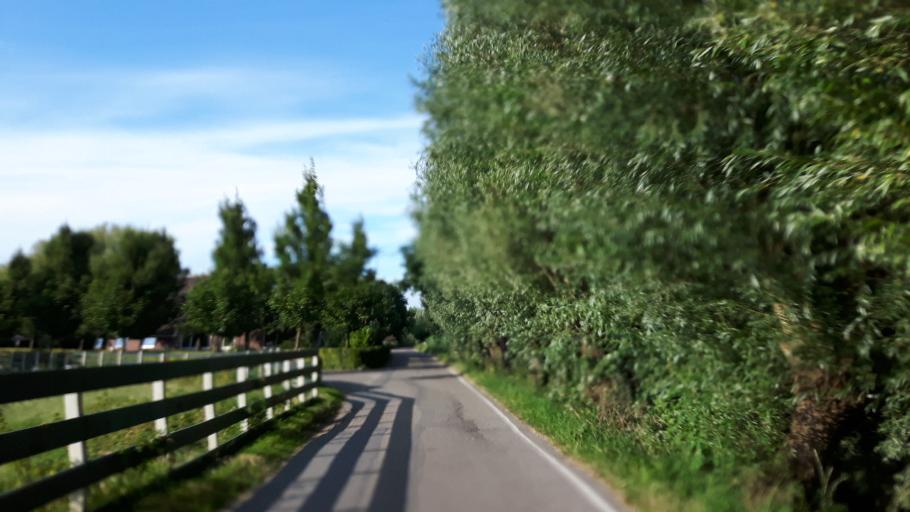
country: NL
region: Utrecht
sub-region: Gemeente Oudewater
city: Oudewater
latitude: 52.0432
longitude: 4.8936
